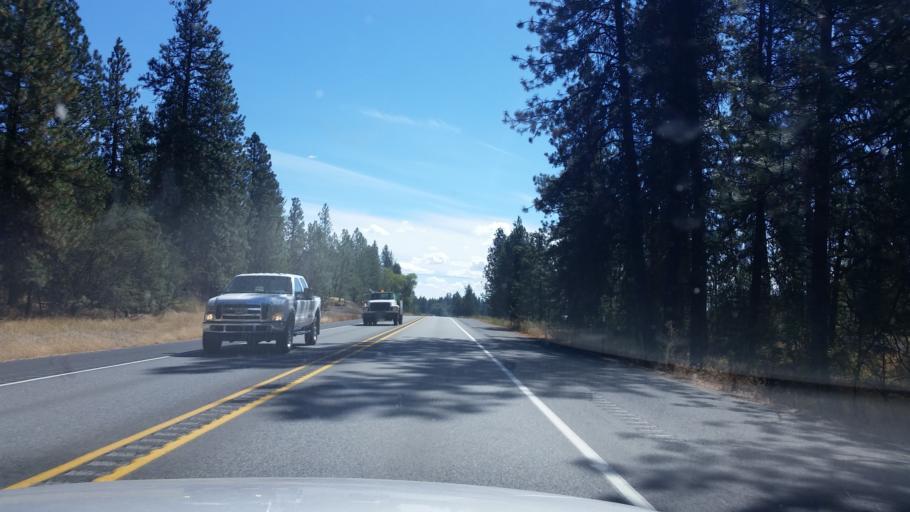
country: US
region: Washington
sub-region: Spokane County
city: Cheney
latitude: 47.5351
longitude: -117.5748
